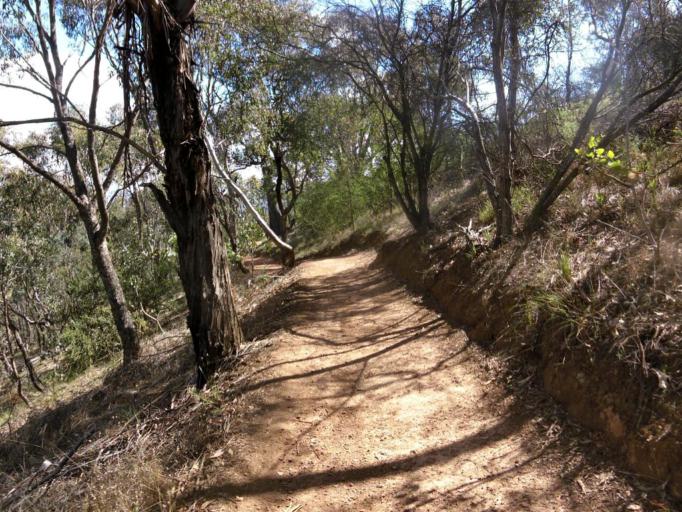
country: AU
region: Australian Capital Territory
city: Belconnen
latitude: -35.1544
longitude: 149.0845
